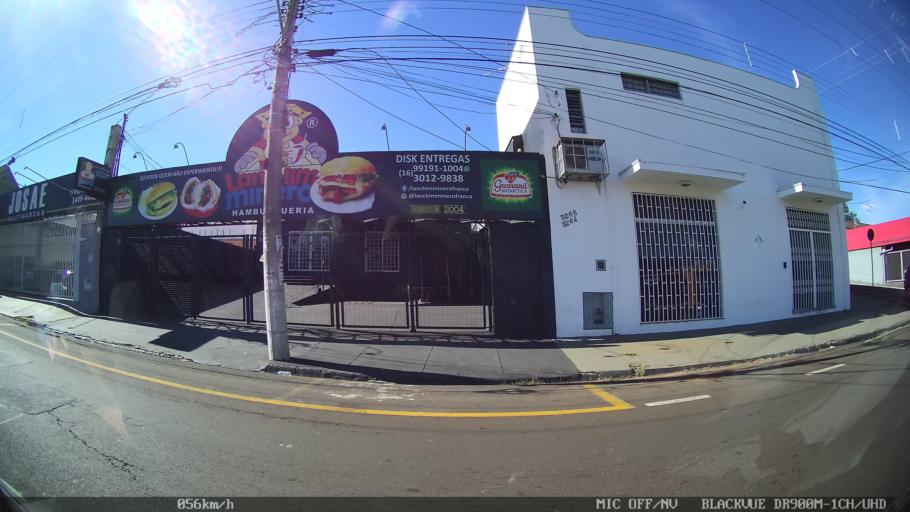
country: BR
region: Sao Paulo
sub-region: Franca
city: Franca
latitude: -20.5249
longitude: -47.4012
